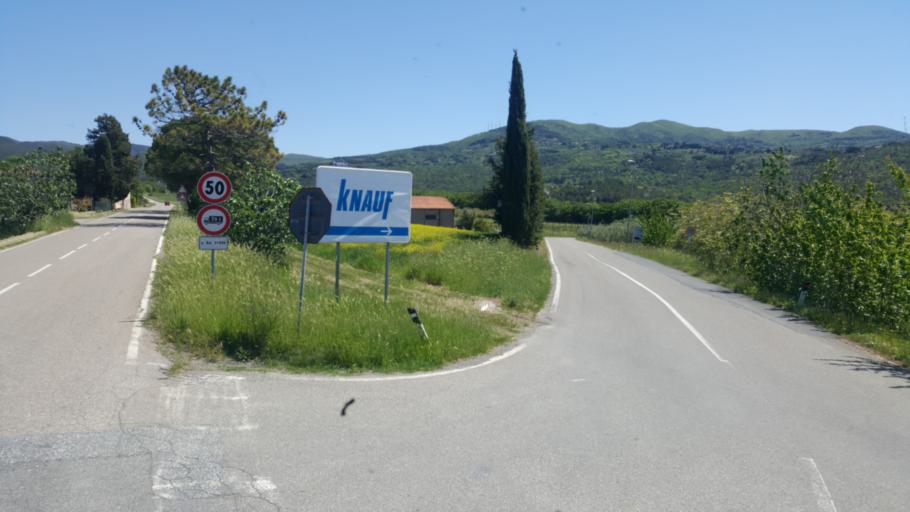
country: IT
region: Tuscany
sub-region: Province of Pisa
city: Castellina Marittima
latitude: 43.4254
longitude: 10.5424
